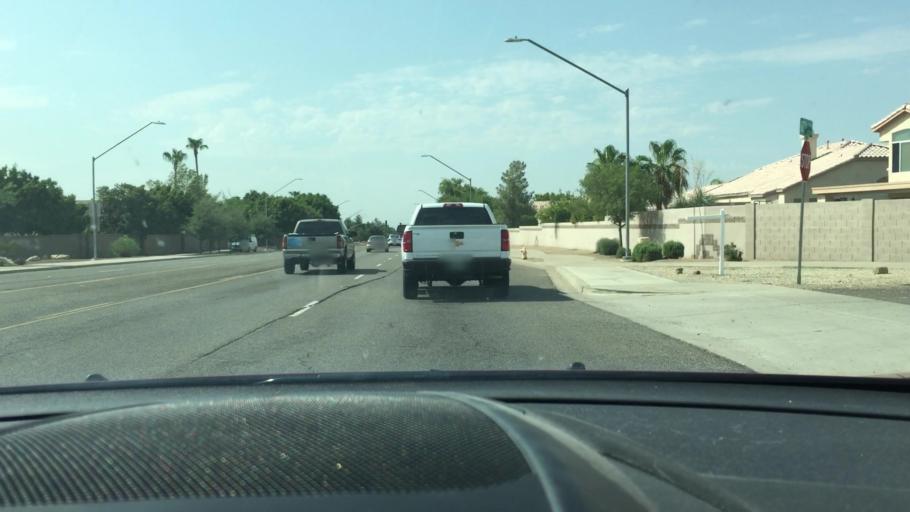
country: US
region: Arizona
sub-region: Maricopa County
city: Peoria
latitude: 33.6873
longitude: -112.2032
